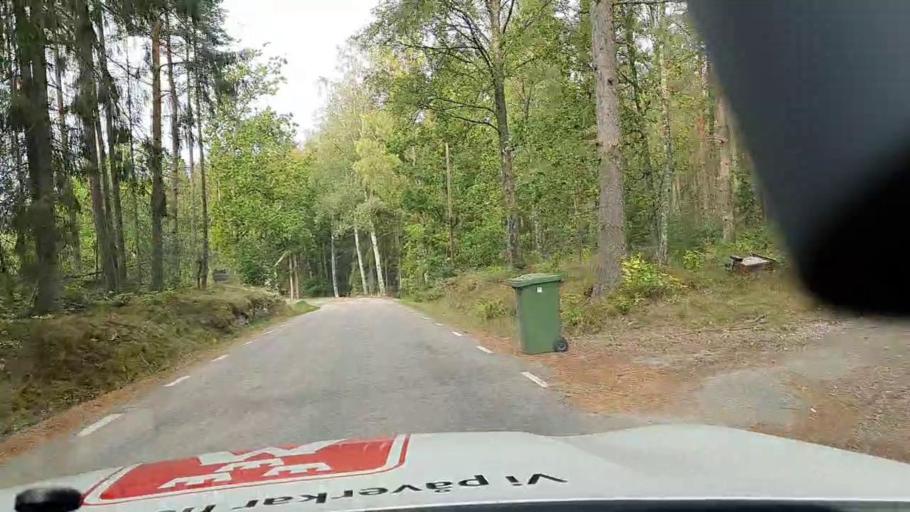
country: SE
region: Soedermanland
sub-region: Nykopings Kommun
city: Svalsta
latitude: 58.8307
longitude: 16.8804
